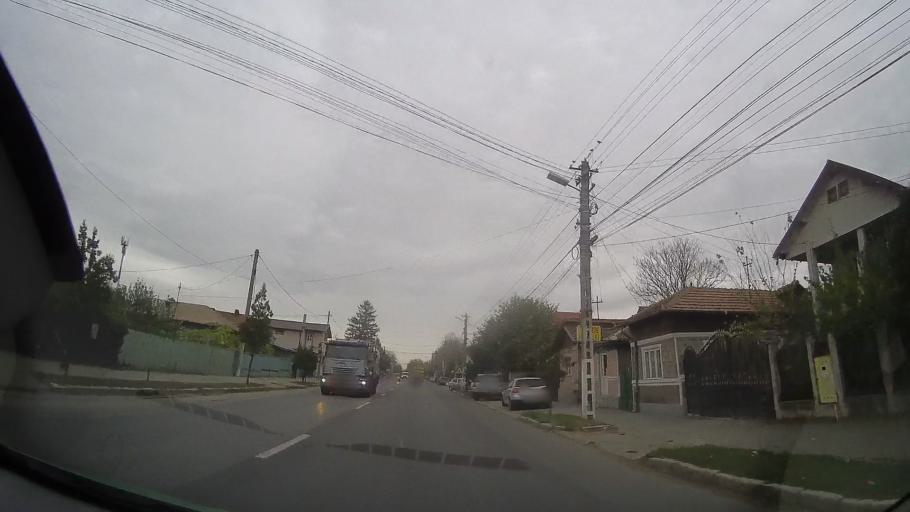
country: RO
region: Prahova
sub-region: Oras Mizil
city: Mizil
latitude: 45.0014
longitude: 26.4387
